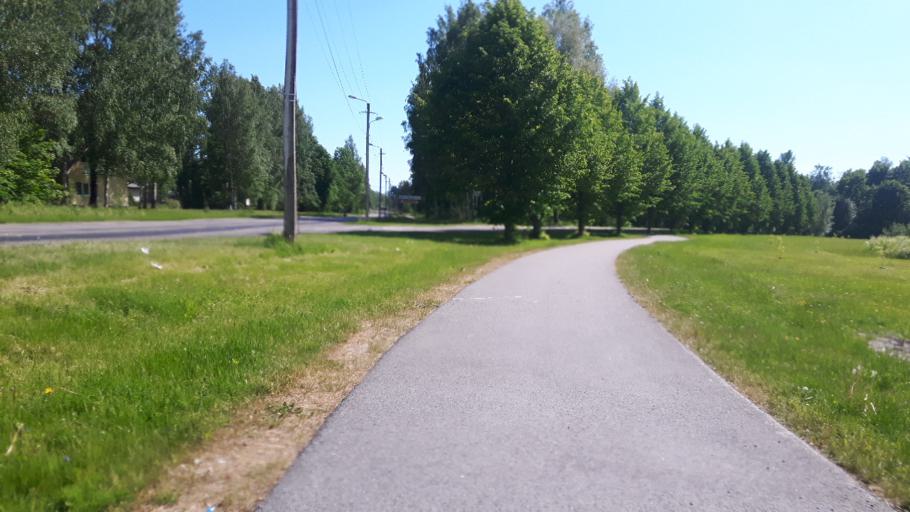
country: EE
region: Paernumaa
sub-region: Paikuse vald
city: Paikuse
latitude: 58.3951
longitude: 24.6408
